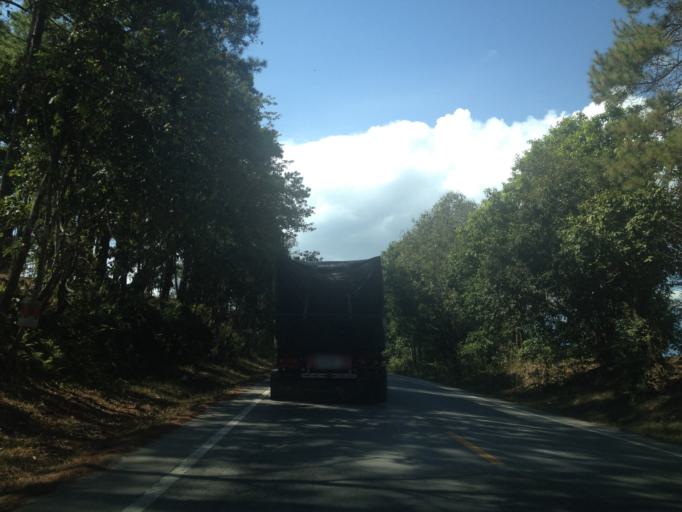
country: TH
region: Chiang Mai
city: Hot
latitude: 18.1395
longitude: 98.3290
